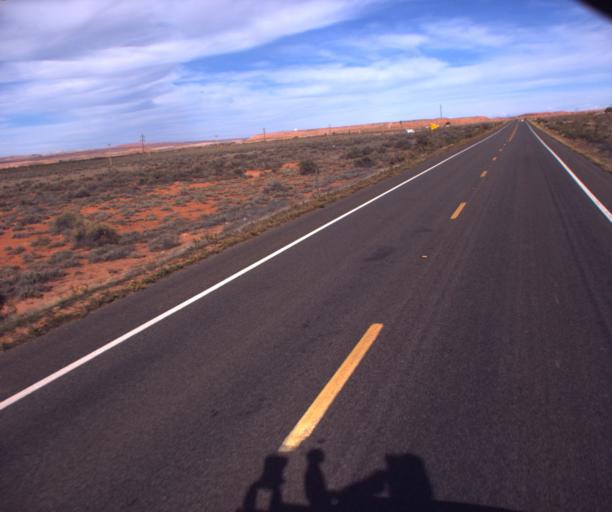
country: US
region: Arizona
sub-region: Navajo County
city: Kayenta
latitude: 36.8120
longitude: -109.8972
